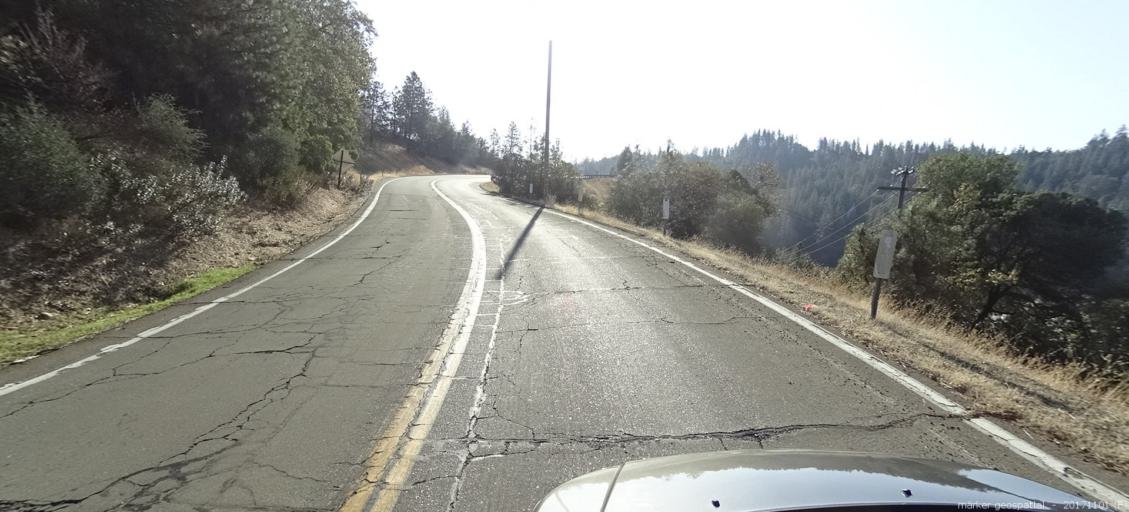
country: US
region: California
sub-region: Shasta County
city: Shasta Lake
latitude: 40.7532
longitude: -122.3229
